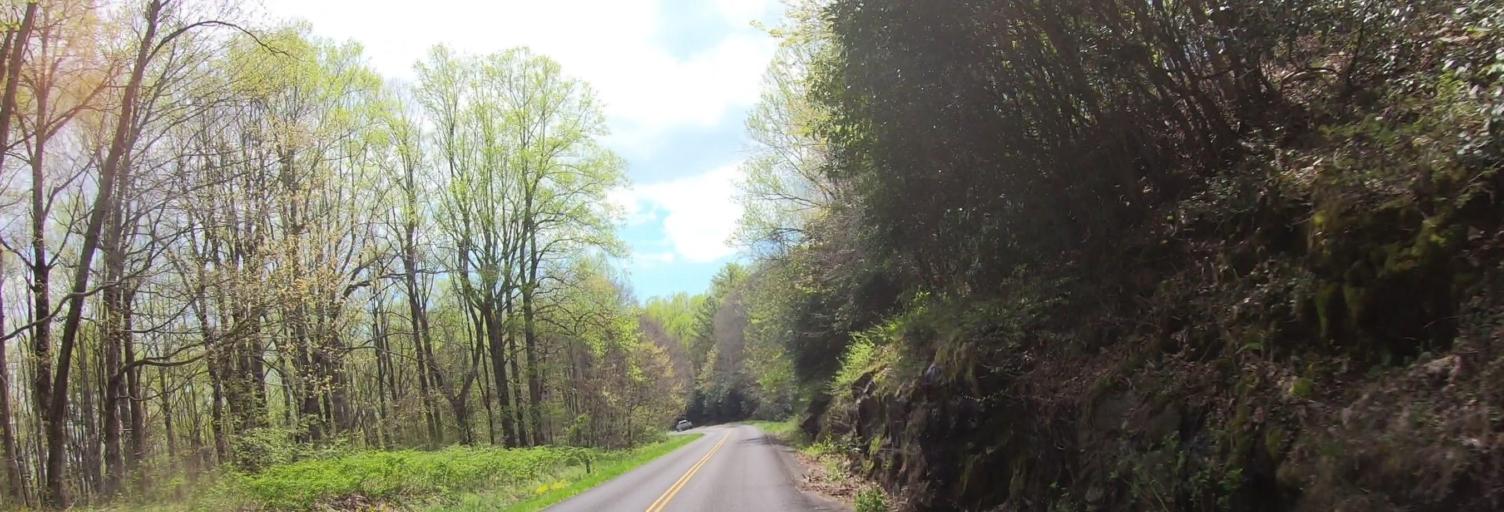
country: US
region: Virginia
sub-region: Carroll County
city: Cana
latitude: 36.6722
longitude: -80.6391
